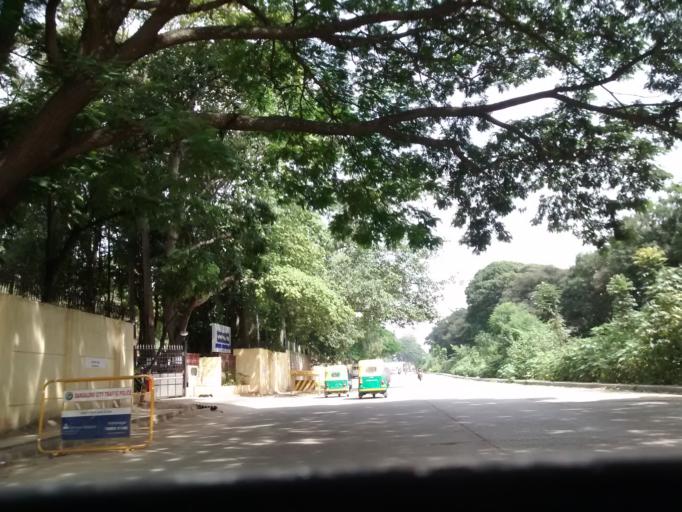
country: IN
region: Karnataka
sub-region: Bangalore Urban
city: Bangalore
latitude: 12.9780
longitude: 77.6537
